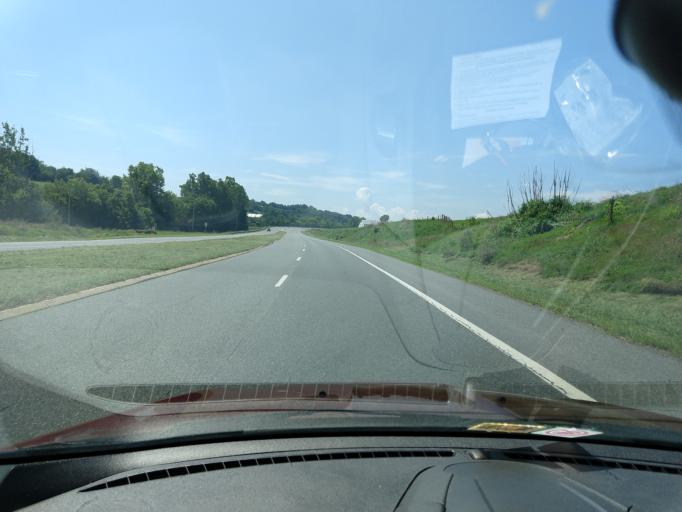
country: US
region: Virginia
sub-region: City of Harrisonburg
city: Harrisonburg
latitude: 38.5234
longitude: -78.8623
